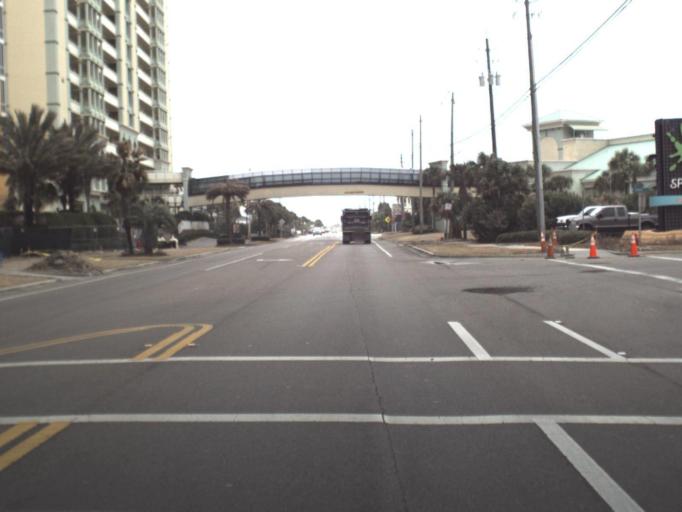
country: US
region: Florida
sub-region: Bay County
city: Laguna Beach
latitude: 30.2330
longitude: -85.9109
